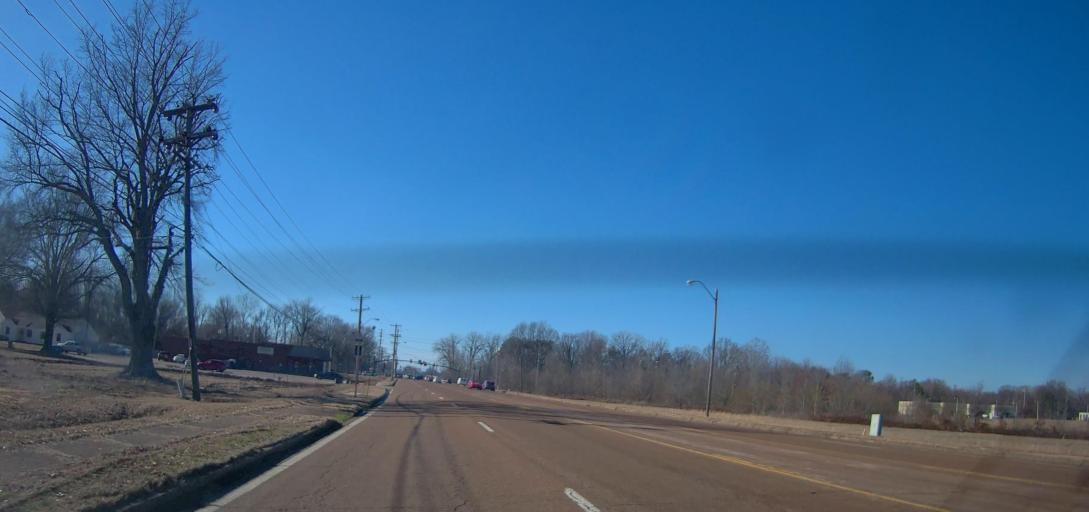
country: US
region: Tennessee
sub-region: Shelby County
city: Millington
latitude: 35.3412
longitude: -89.8860
